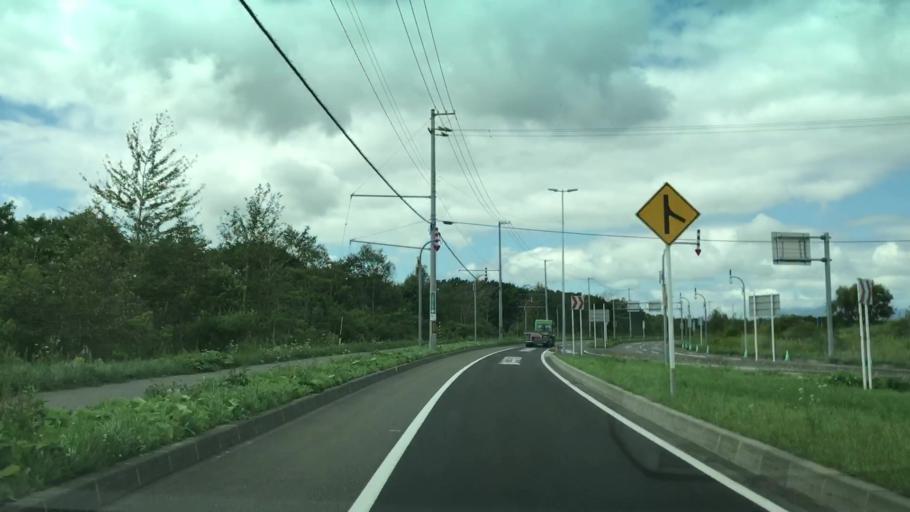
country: JP
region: Hokkaido
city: Chitose
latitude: 42.7752
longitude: 141.6383
